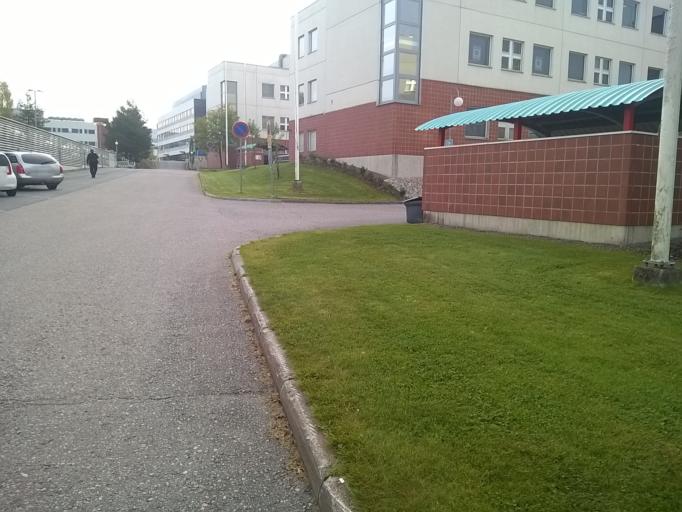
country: FI
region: Pirkanmaa
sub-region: Tampere
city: Tampere
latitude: 61.4465
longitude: 23.8582
